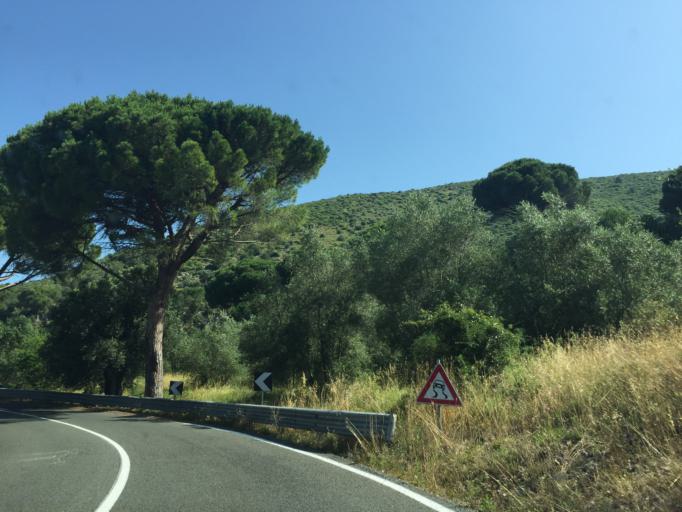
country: IT
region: Tuscany
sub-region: Province of Pisa
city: San Giuliano Terme
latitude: 43.7635
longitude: 10.4468
